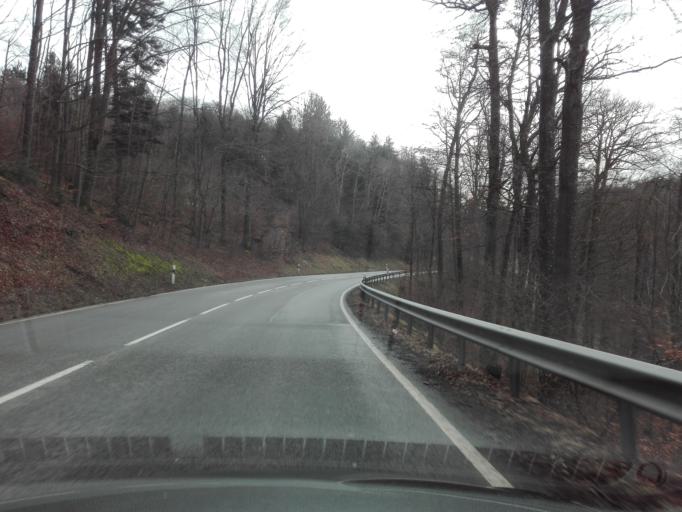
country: DE
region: Bavaria
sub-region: Lower Bavaria
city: Obernzell
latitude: 48.5699
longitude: 13.6447
